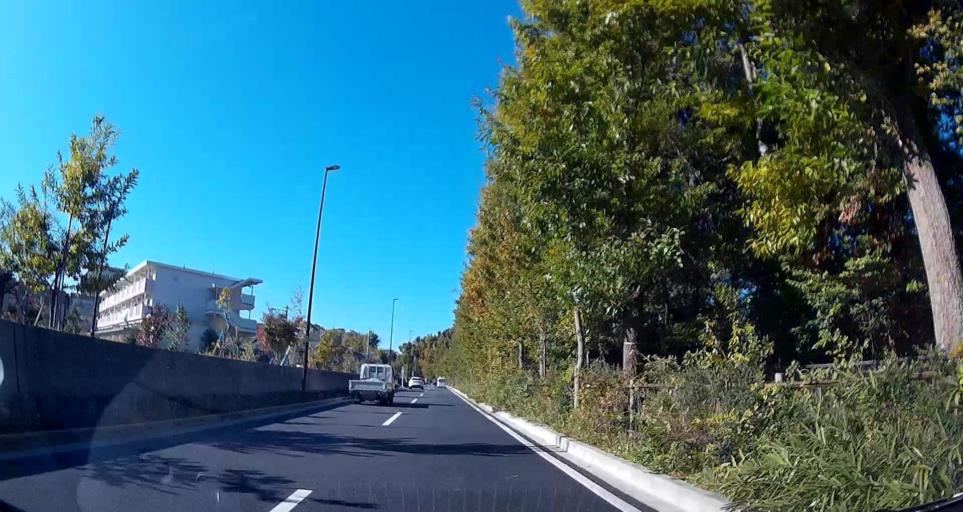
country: JP
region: Tokyo
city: Mitaka-shi
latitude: 35.6825
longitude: 139.6005
